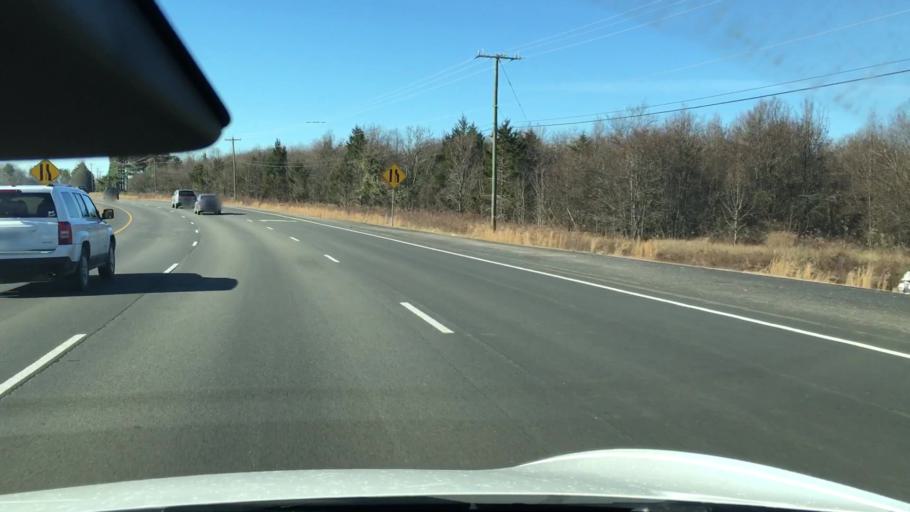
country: US
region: Virginia
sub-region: Chesterfield County
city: Woodlake
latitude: 37.5071
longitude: -77.6984
